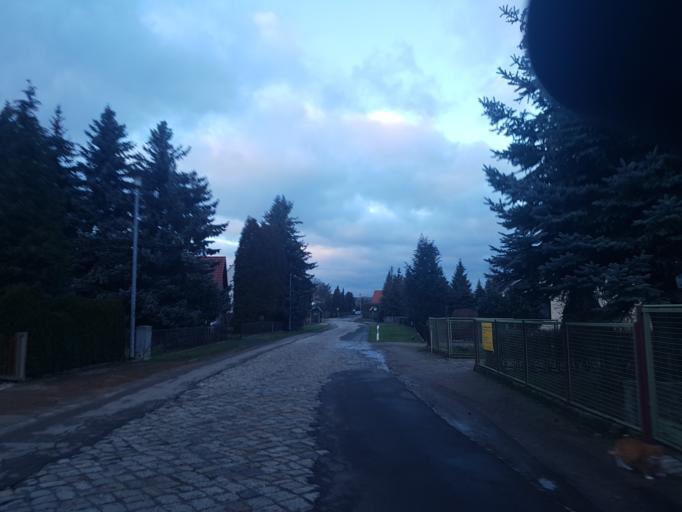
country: DE
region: Brandenburg
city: Muhlberg
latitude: 51.4678
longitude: 13.2038
